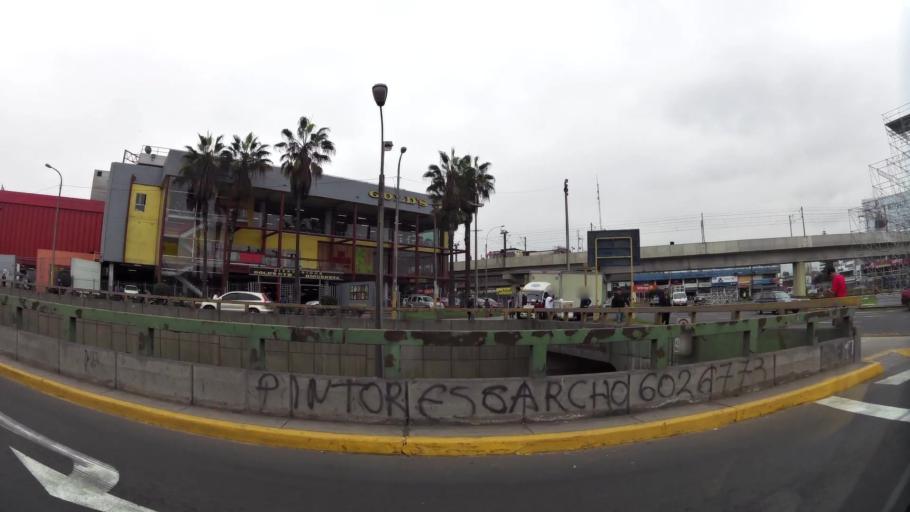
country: PE
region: Lima
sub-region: Lima
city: Surco
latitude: -12.1284
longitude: -77.0016
